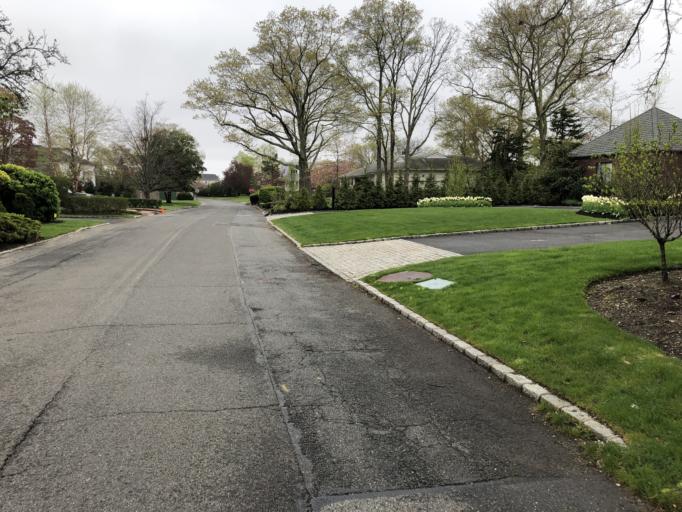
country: US
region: New York
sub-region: Nassau County
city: Hewlett Harbor
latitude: 40.6347
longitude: -73.6905
